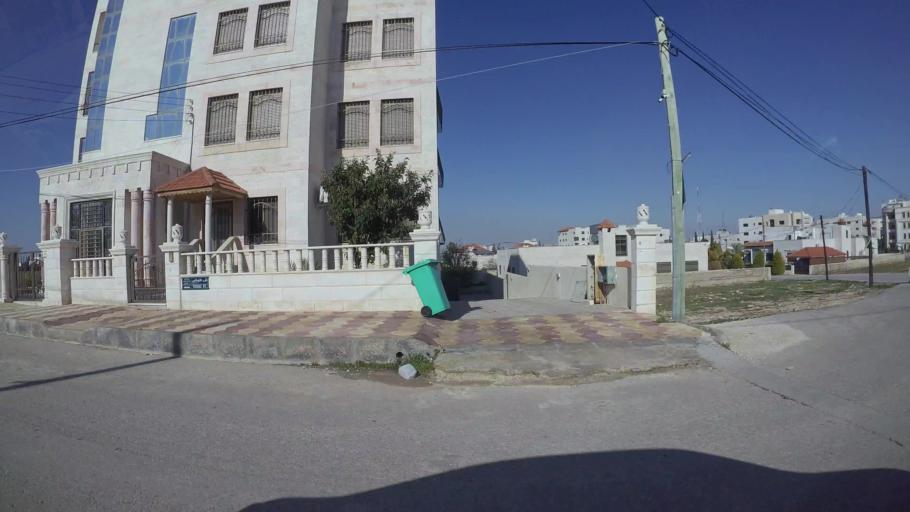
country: JO
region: Amman
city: Al Bunayyat ash Shamaliyah
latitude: 31.9024
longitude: 35.9200
